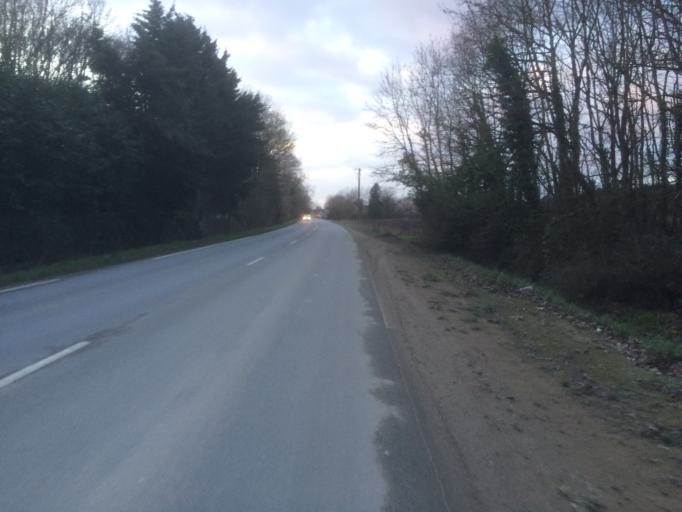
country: FR
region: Ile-de-France
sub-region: Departement de l'Essonne
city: Orsay
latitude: 48.6673
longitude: 2.2024
